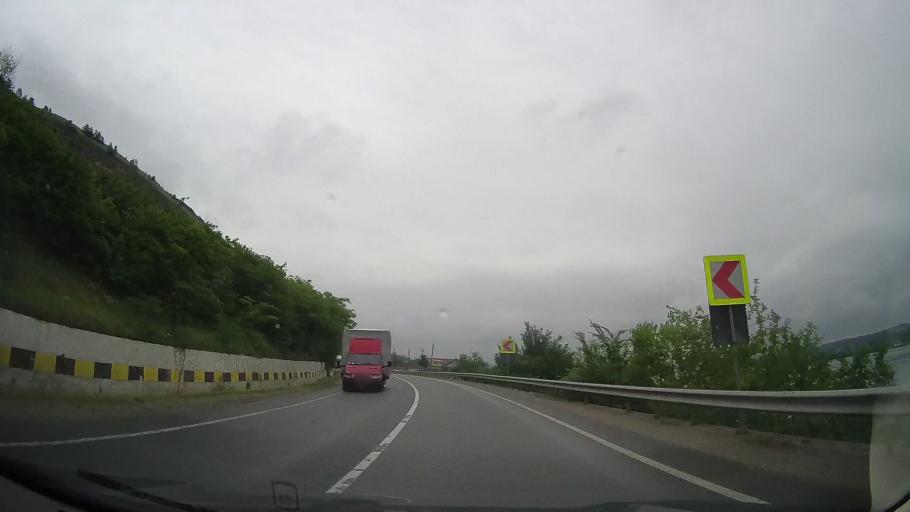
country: RO
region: Mehedinti
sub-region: Municipiul Drobeta-Turnu Severin
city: Gura Vaii
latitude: 44.6408
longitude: 22.5777
